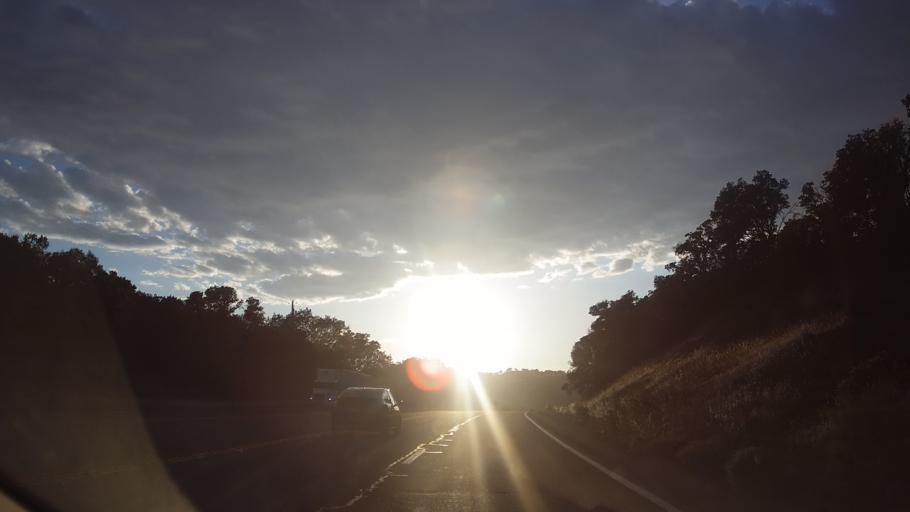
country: US
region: California
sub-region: Mendocino County
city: Redwood Valley
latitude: 39.2725
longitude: -123.2475
